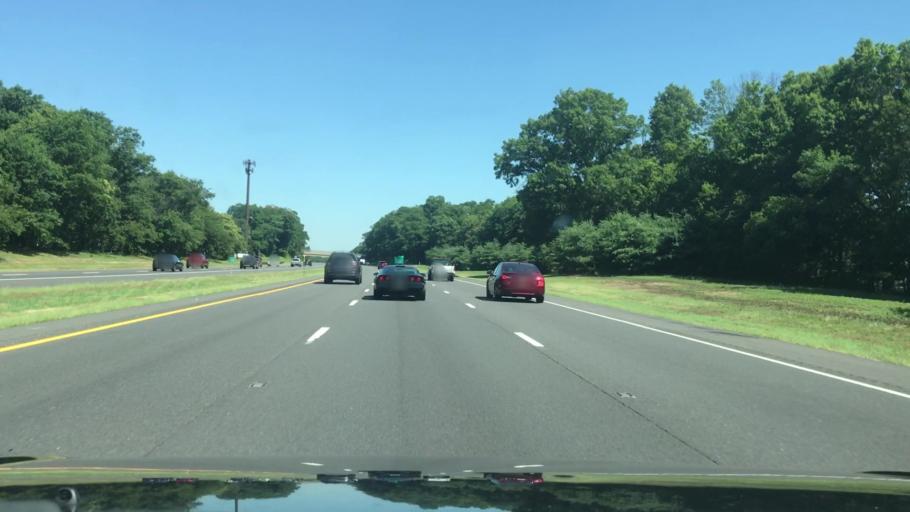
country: US
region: New Jersey
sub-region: Monmouth County
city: Tinton Falls
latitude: 40.3058
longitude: -74.0932
